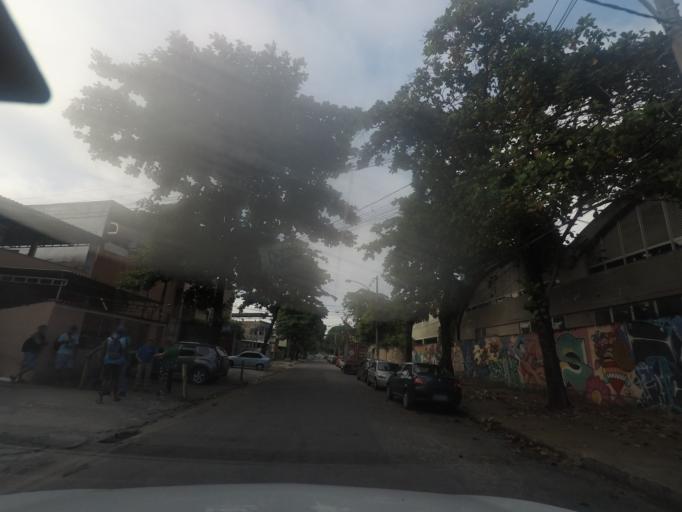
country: BR
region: Rio de Janeiro
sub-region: Duque De Caxias
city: Duque de Caxias
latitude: -22.8303
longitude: -43.2718
